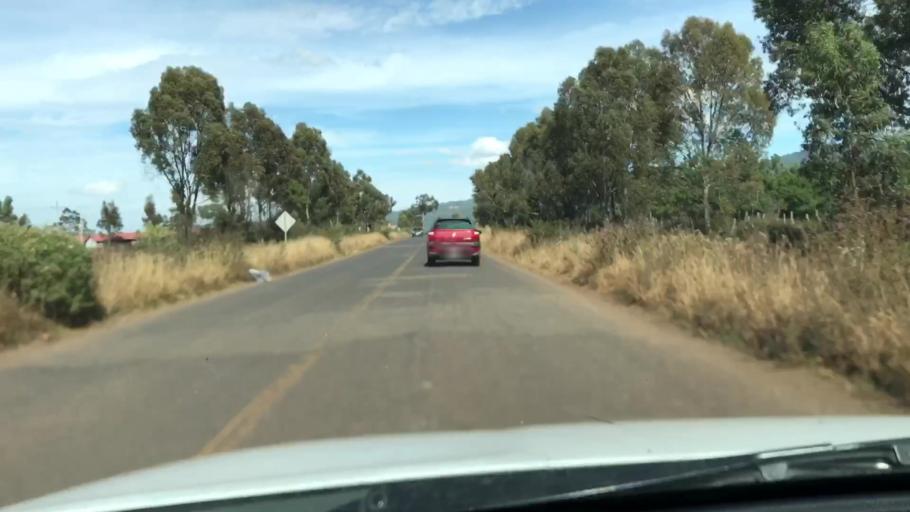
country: MX
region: Jalisco
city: Chiquilistlan
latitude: 20.1276
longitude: -103.7224
